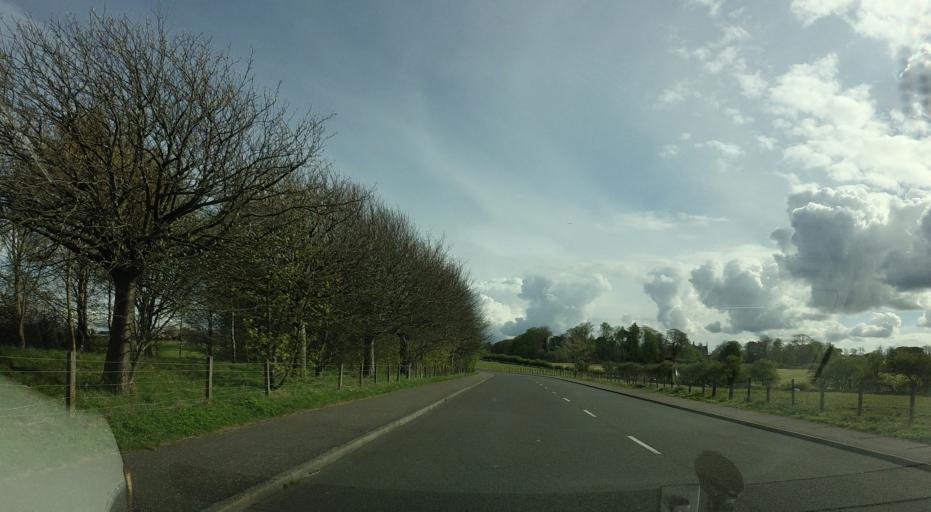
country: GB
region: Scotland
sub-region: Edinburgh
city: Colinton
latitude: 55.9752
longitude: -3.2772
